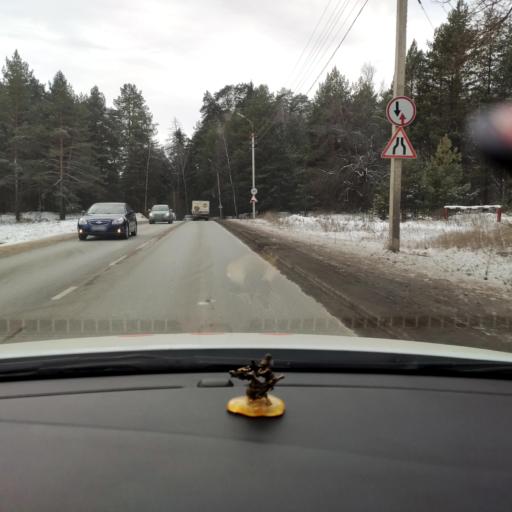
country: RU
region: Tatarstan
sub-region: Zelenodol'skiy Rayon
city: Zelenodolsk
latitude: 55.8640
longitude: 48.5359
